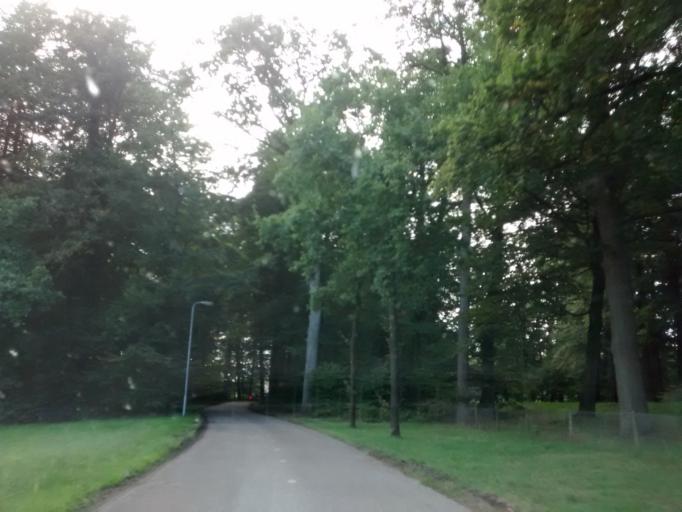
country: NL
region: Overijssel
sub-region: Gemeente Oldenzaal
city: Oldenzaal
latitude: 52.3198
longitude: 6.9632
